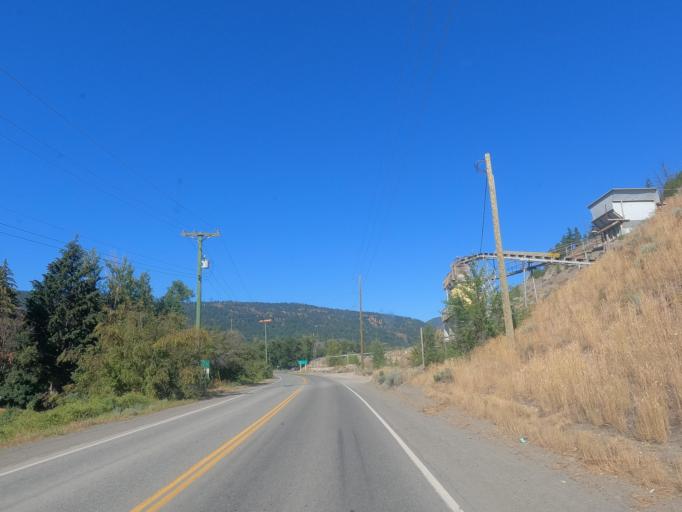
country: CA
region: British Columbia
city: Merritt
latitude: 50.1159
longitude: -120.8017
